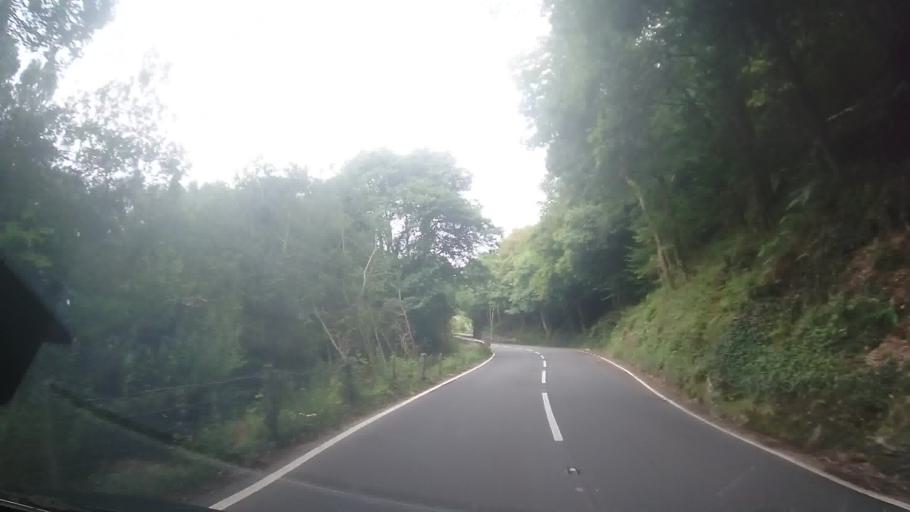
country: GB
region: Wales
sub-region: Gwynedd
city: Barmouth
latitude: 52.7044
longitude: -4.0235
